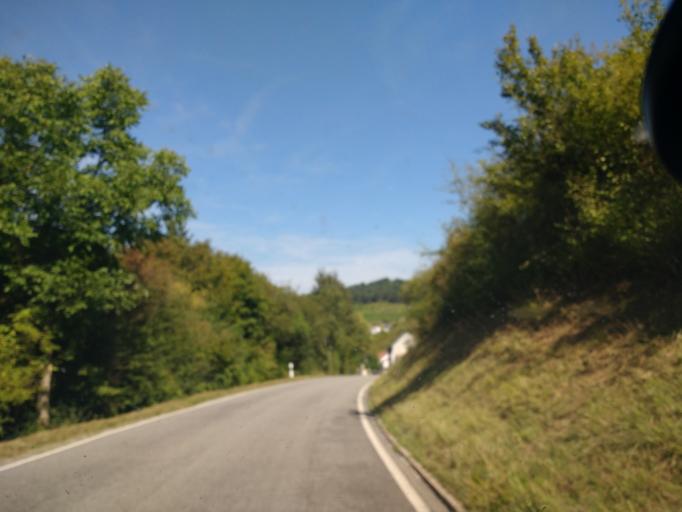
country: DE
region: Rheinland-Pfalz
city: Nittel
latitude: 49.6479
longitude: 6.4533
